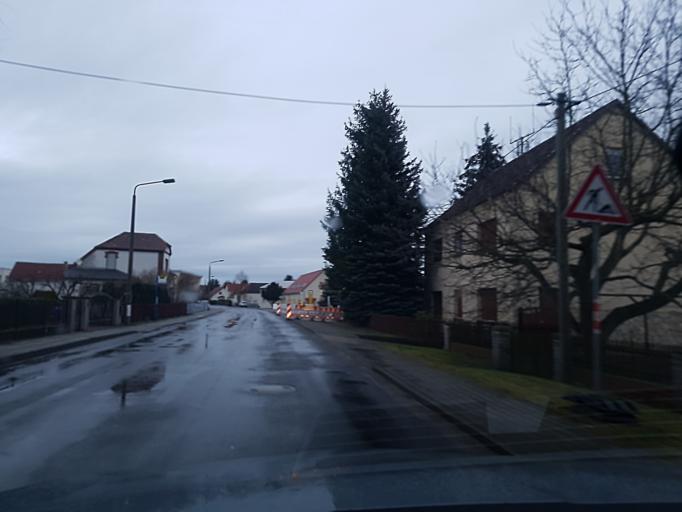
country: DE
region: Brandenburg
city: Falkenberg
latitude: 51.5972
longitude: 13.3056
